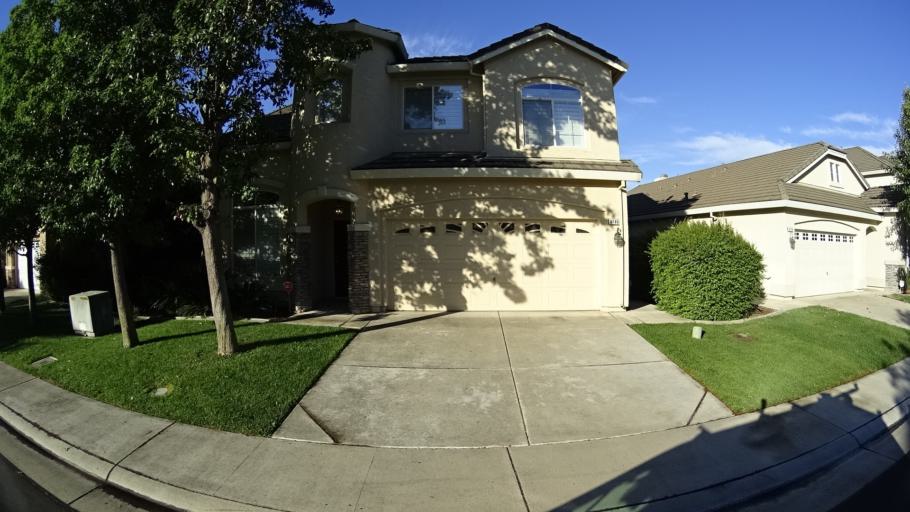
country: US
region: California
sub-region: Sacramento County
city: Laguna
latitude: 38.4031
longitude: -121.4788
